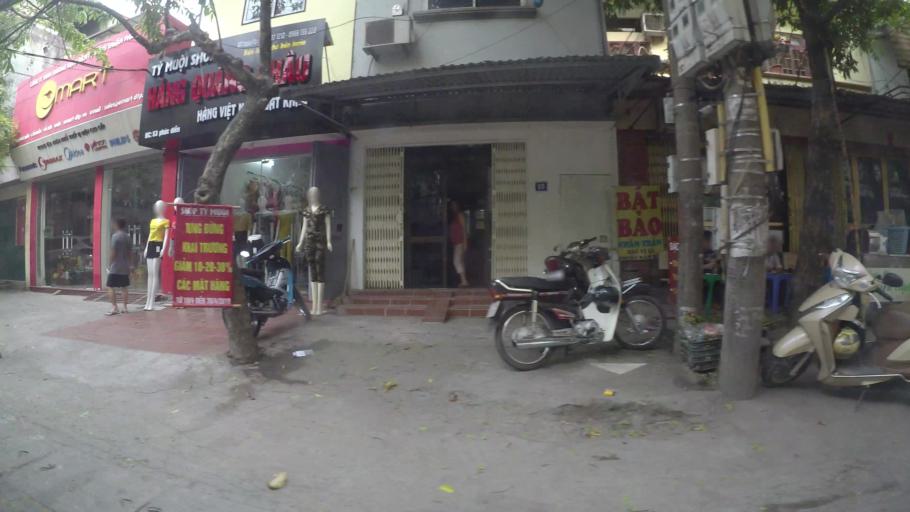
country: VN
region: Ha Noi
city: Cau Dien
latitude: 21.0404
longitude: 105.7604
